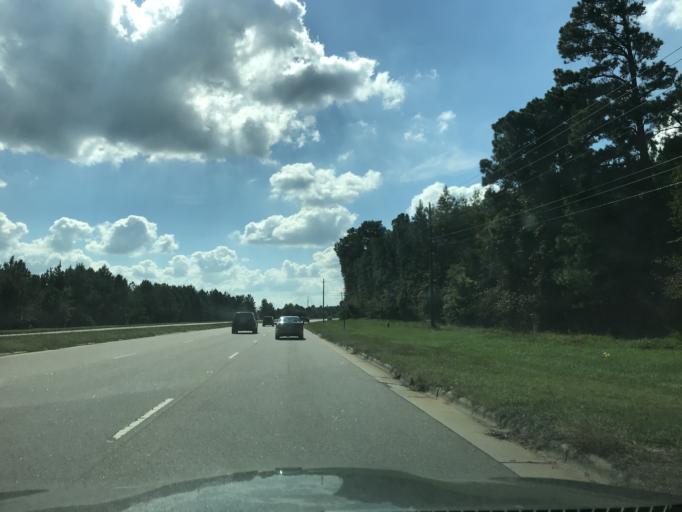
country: US
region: North Carolina
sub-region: Wake County
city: Rolesville
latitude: 35.8812
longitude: -78.5316
